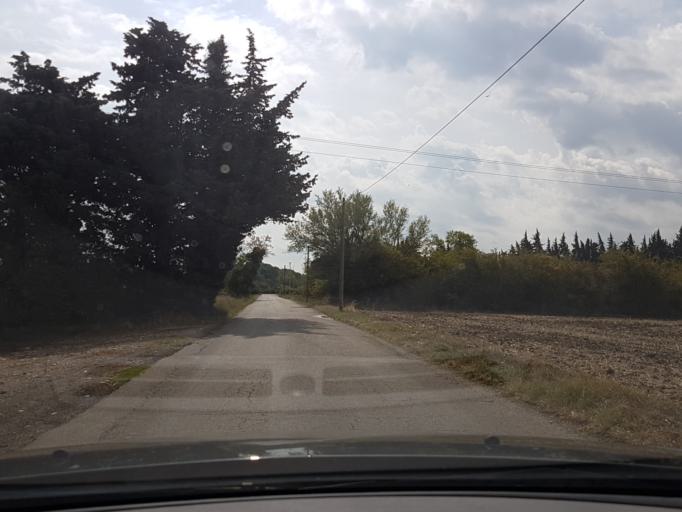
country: FR
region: Provence-Alpes-Cote d'Azur
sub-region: Departement du Vaucluse
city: Saint-Saturnin-les-Avignon
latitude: 43.9697
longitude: 4.9387
